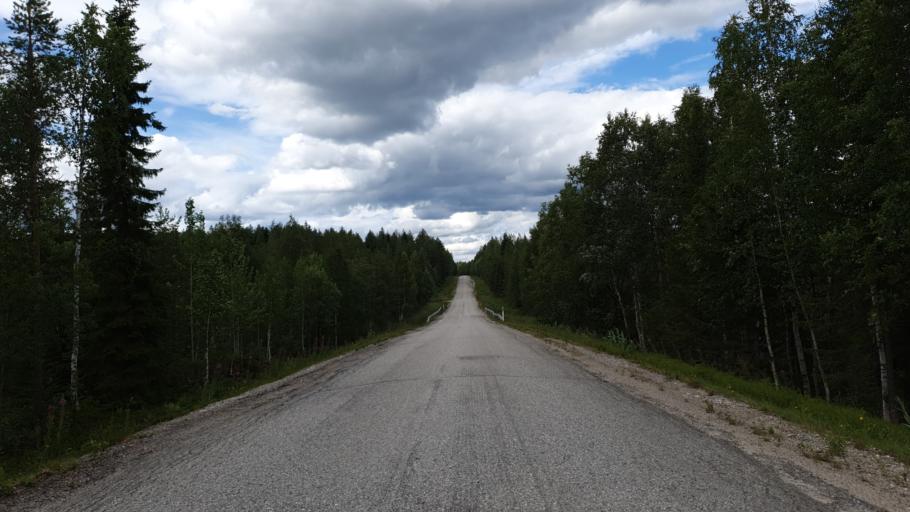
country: FI
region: Kainuu
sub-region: Kehys-Kainuu
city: Kuhmo
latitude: 64.4400
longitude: 29.7052
